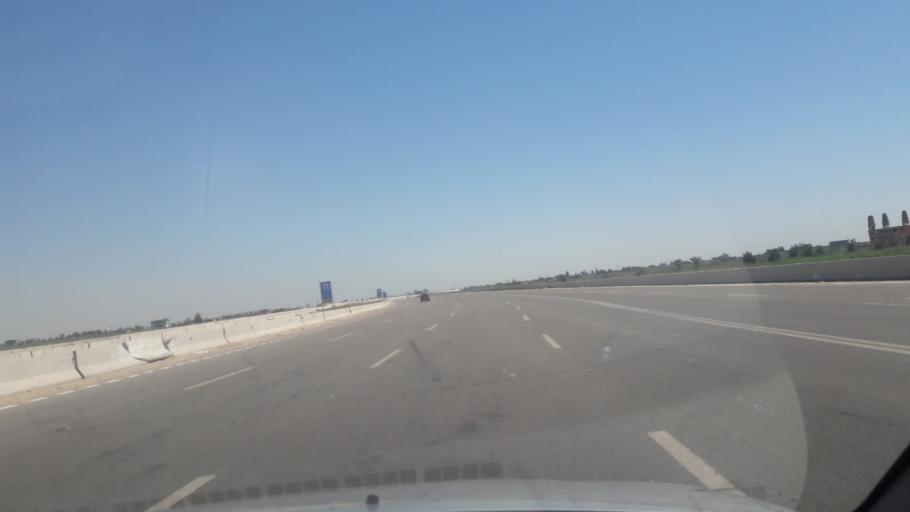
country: EG
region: Muhafazat Bur Sa`id
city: Port Said
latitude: 31.0710
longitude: 32.2348
